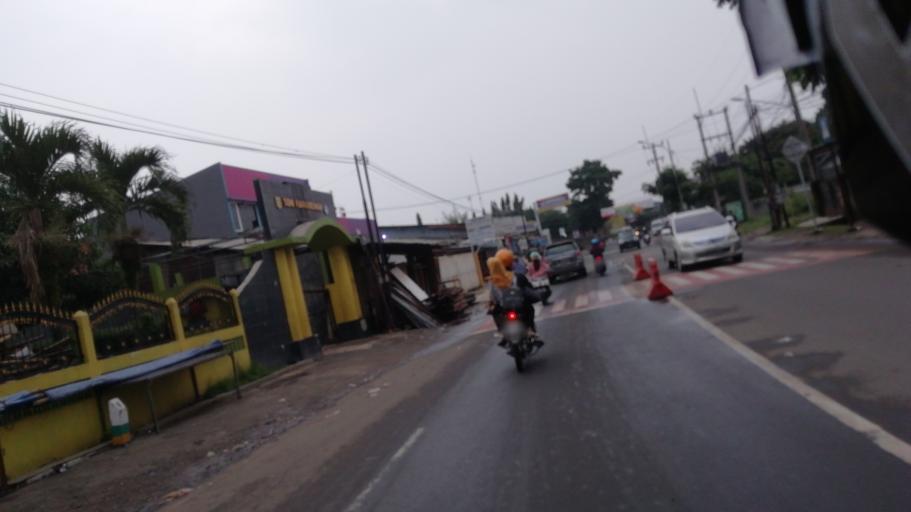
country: ID
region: West Java
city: Cibinong
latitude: -6.5066
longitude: 106.8065
